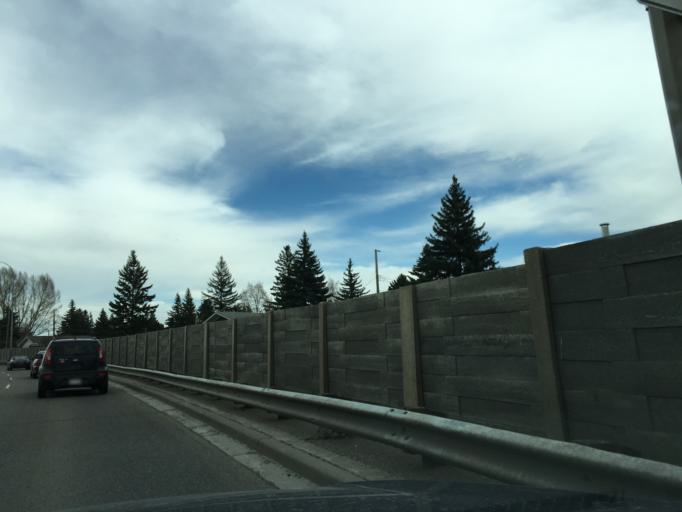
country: CA
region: Alberta
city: Calgary
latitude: 50.9640
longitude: -114.0446
